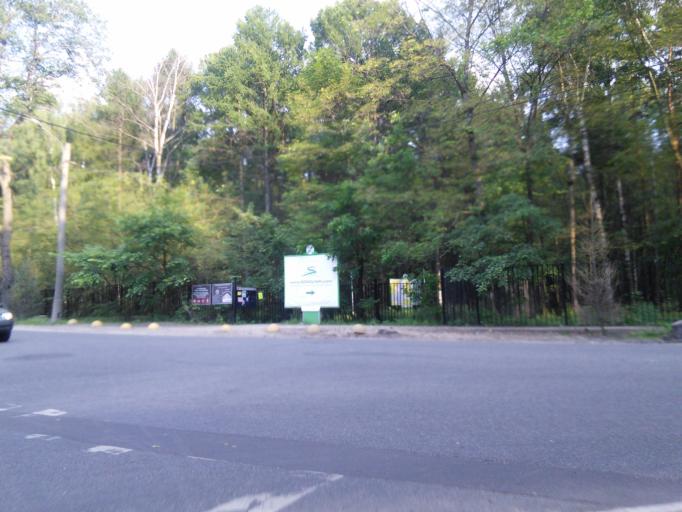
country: RU
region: Moscow
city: Sokol'niki
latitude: 55.8078
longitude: 37.6746
